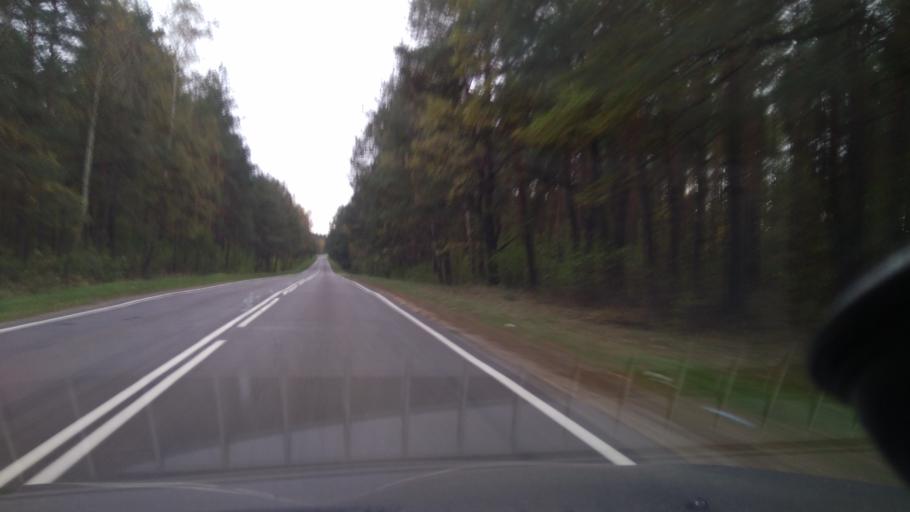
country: BY
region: Minsk
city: Druzhny
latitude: 53.6386
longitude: 27.9010
